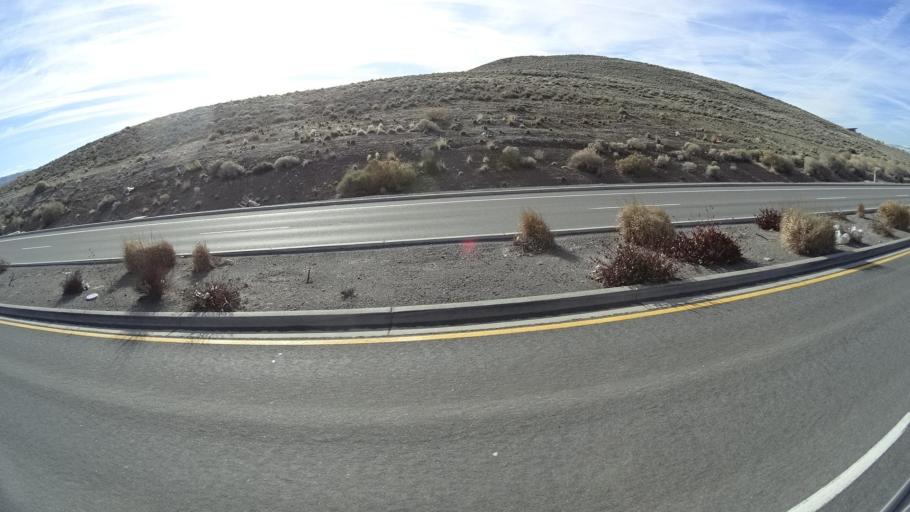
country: US
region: Nevada
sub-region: Washoe County
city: Spanish Springs
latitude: 39.5994
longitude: -119.7124
